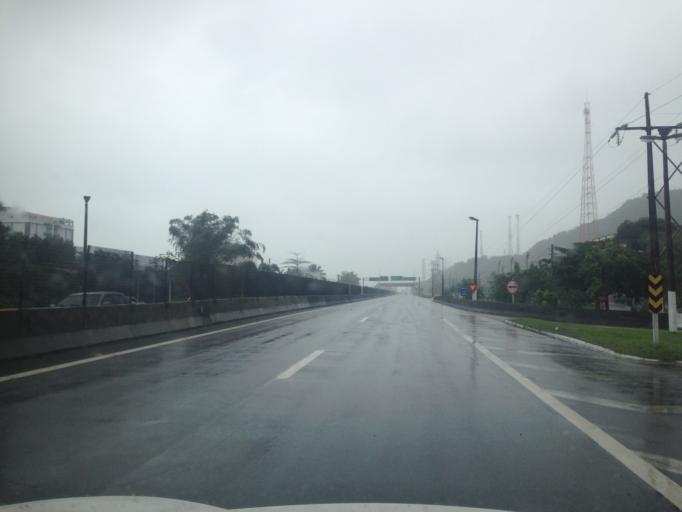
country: BR
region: Sao Paulo
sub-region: Mongagua
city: Mongagua
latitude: -24.0947
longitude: -46.6253
